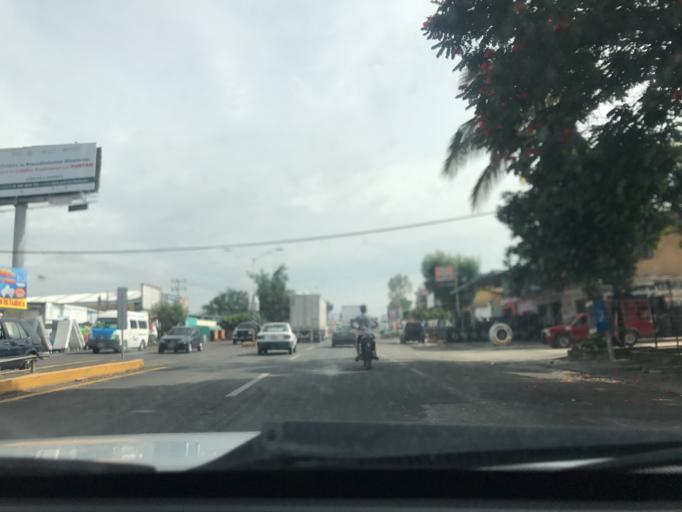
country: MX
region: Morelos
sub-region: Cuautla
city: Tierra Larga (Campo Nuevo)
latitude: 18.8582
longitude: -98.9348
